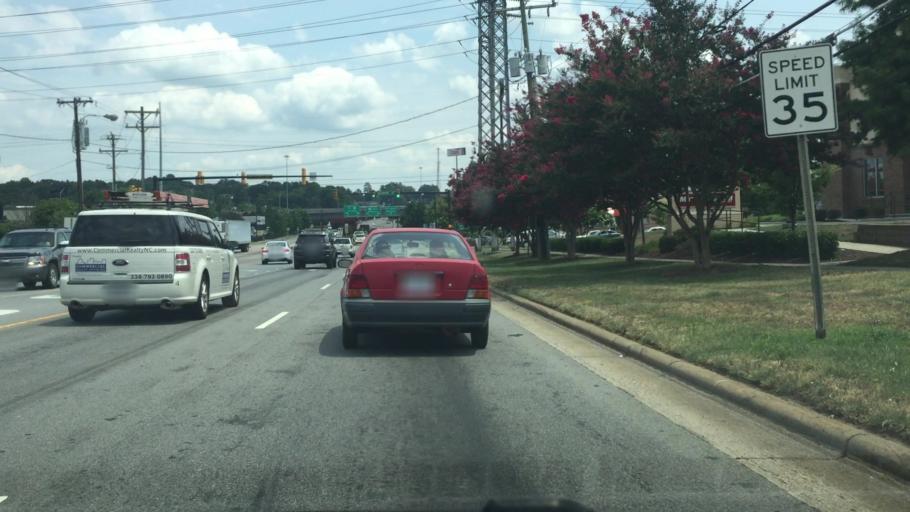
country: US
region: North Carolina
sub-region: Rowan County
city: Salisbury
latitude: 35.6606
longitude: -80.4626
